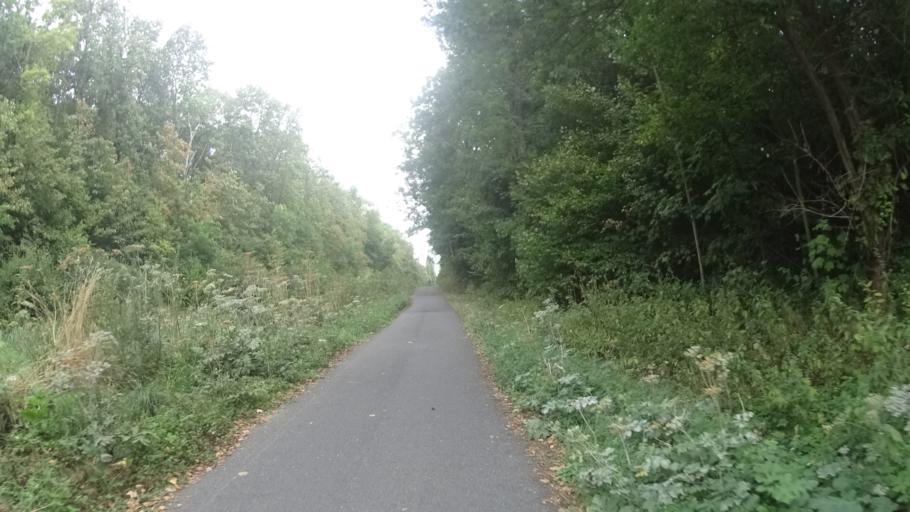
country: FR
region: Ile-de-France
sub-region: Departement de Seine-et-Marne
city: Villeparisis
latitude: 48.9500
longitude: 2.5938
